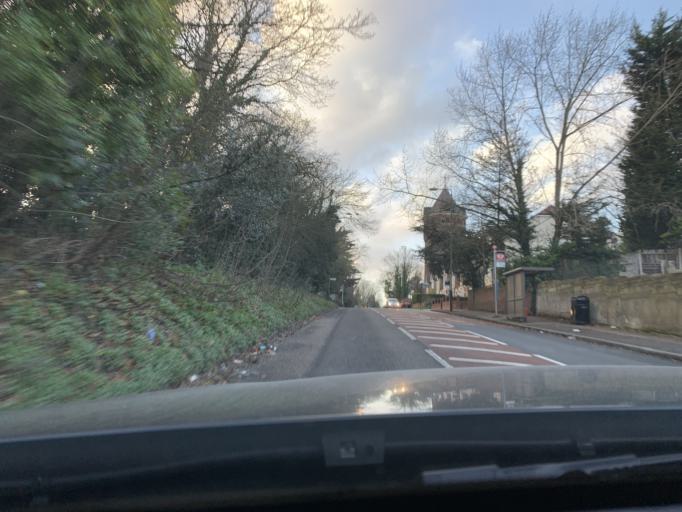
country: GB
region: England
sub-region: Greater London
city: Woolwich
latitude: 51.4686
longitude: 0.0705
